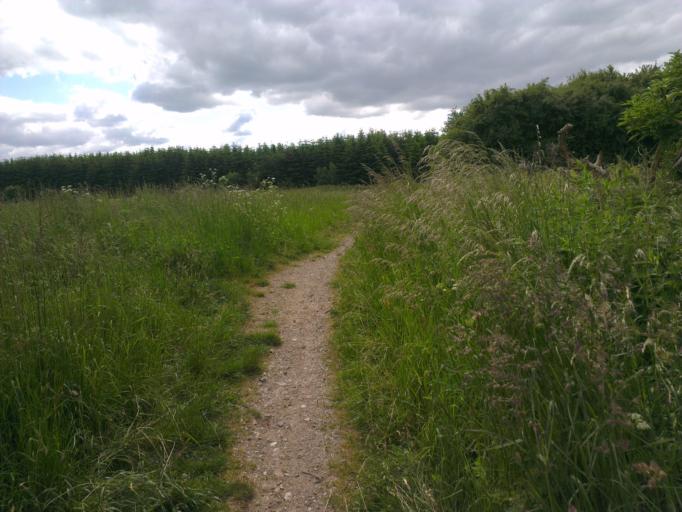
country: DK
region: Capital Region
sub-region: Frederikssund Kommune
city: Slangerup
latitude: 55.8503
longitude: 12.1900
